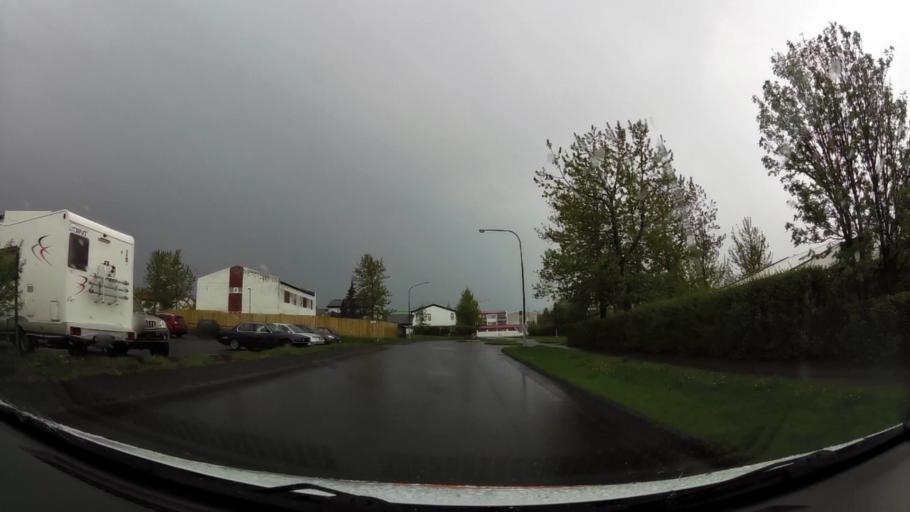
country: IS
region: Capital Region
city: Reykjavik
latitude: 64.1066
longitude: -21.8073
